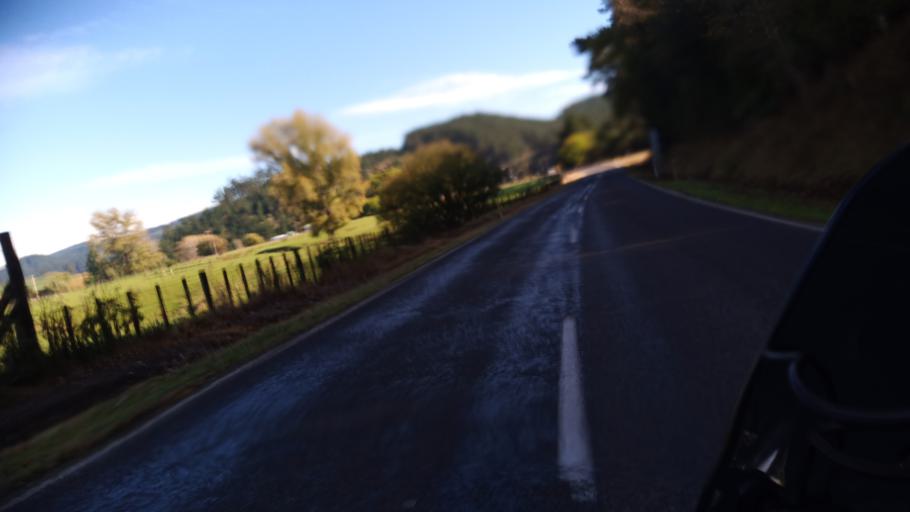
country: NZ
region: Hawke's Bay
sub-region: Wairoa District
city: Wairoa
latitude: -38.9230
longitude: 177.2695
